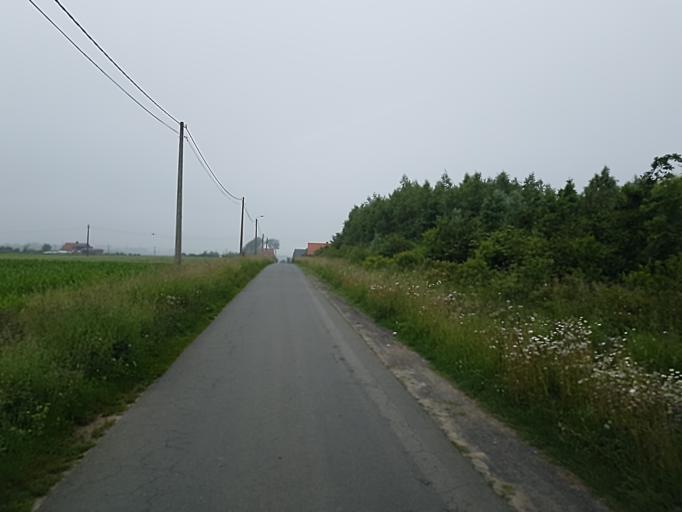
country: BE
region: Flanders
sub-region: Provincie West-Vlaanderen
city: Zonnebeke
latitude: 50.8588
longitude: 2.9795
